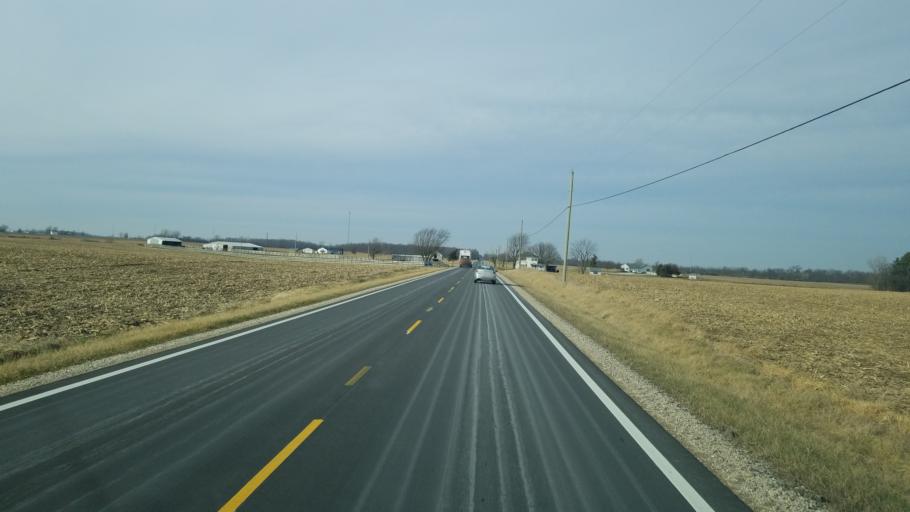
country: US
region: Ohio
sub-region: Union County
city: Richwood
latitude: 40.4291
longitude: -83.4348
